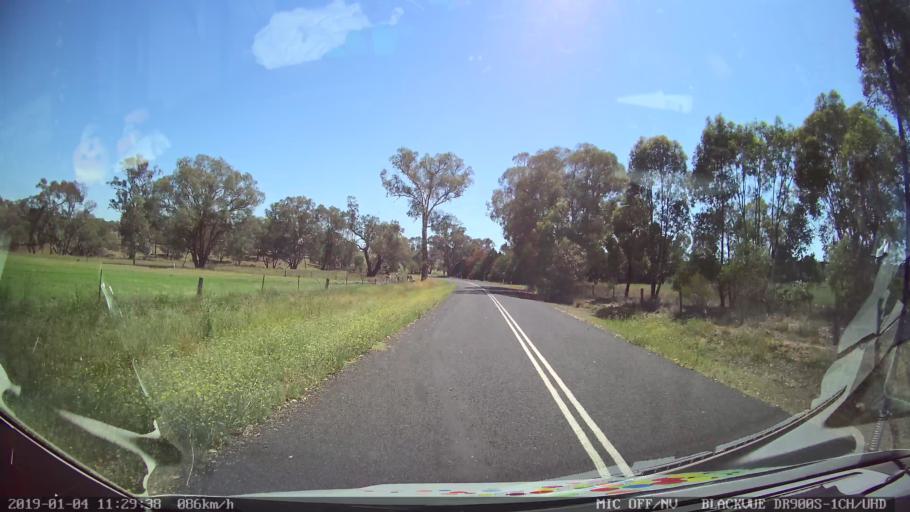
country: AU
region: New South Wales
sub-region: Cabonne
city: Molong
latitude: -33.0857
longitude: 148.7755
